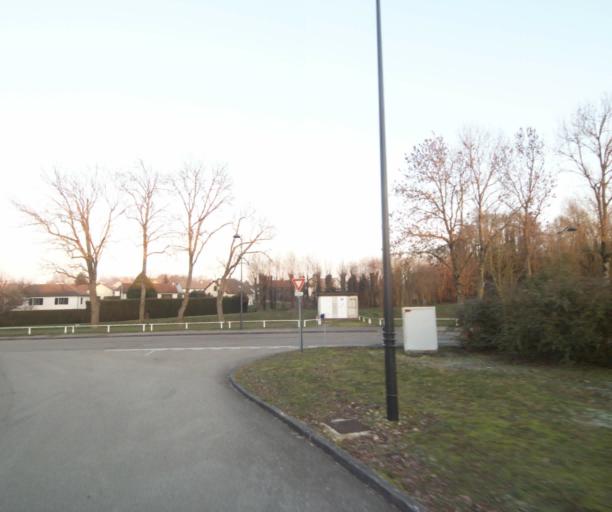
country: FR
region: Champagne-Ardenne
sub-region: Departement de la Haute-Marne
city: Saint-Dizier
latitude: 48.6256
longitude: 4.9720
